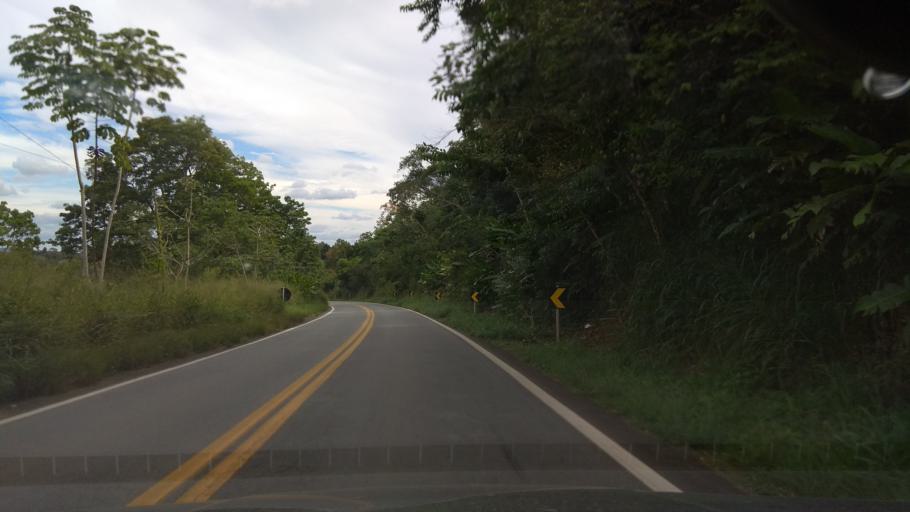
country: BR
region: Bahia
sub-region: Ubata
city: Ubata
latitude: -14.1977
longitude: -39.5670
